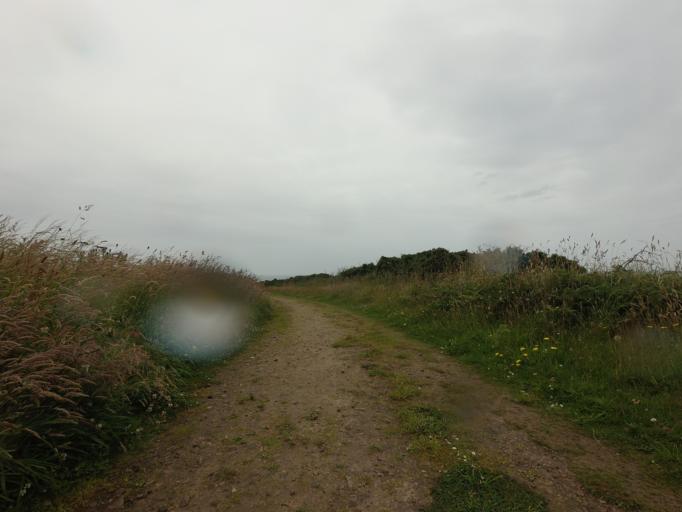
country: GB
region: Scotland
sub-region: Moray
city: Portknockie
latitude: 57.7027
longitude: -2.8747
